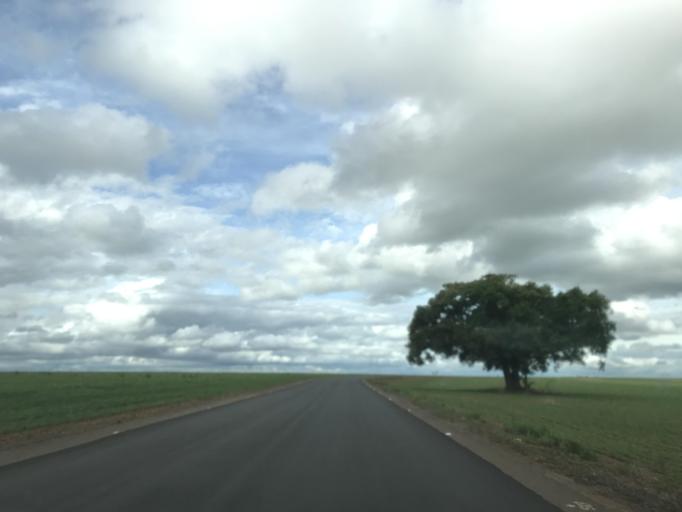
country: BR
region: Goias
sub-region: Vianopolis
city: Vianopolis
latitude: -16.9610
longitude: -48.6395
